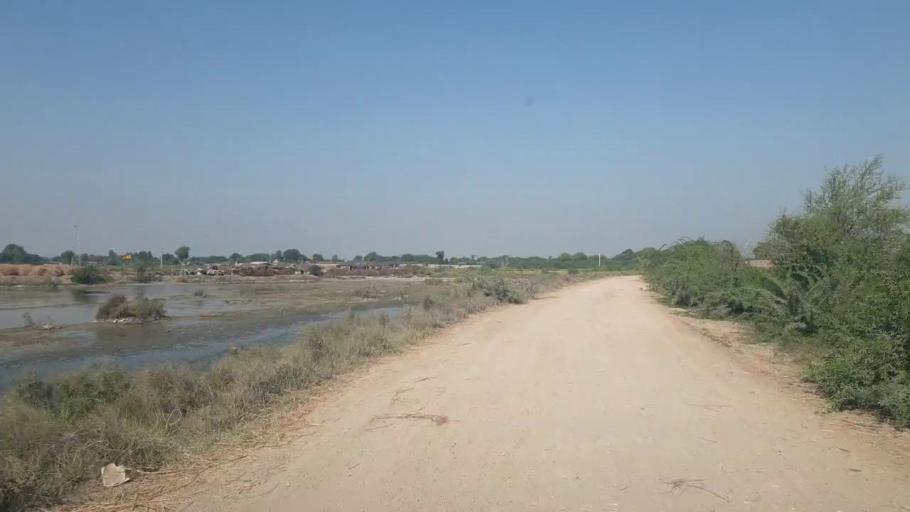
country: PK
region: Sindh
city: Badin
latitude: 24.6749
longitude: 68.8576
